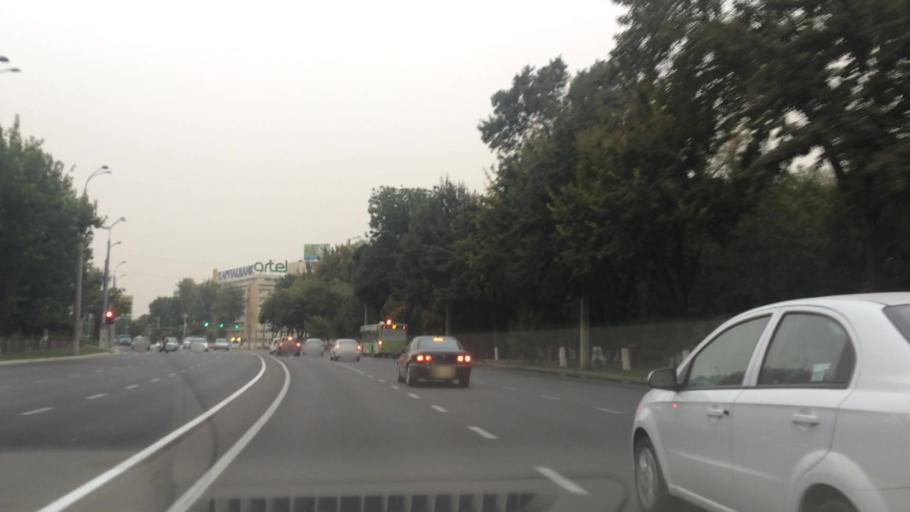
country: UZ
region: Toshkent Shahri
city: Tashkent
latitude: 41.3036
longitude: 69.2681
